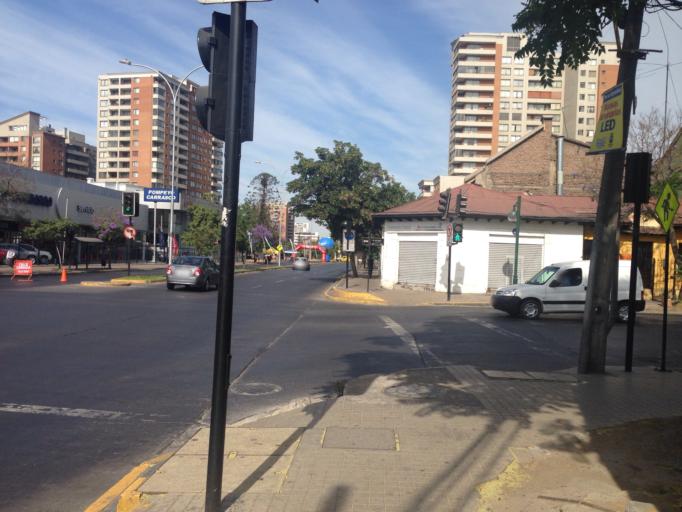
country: CL
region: Santiago Metropolitan
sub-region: Provincia de Santiago
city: Santiago
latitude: -33.4534
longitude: -70.6205
